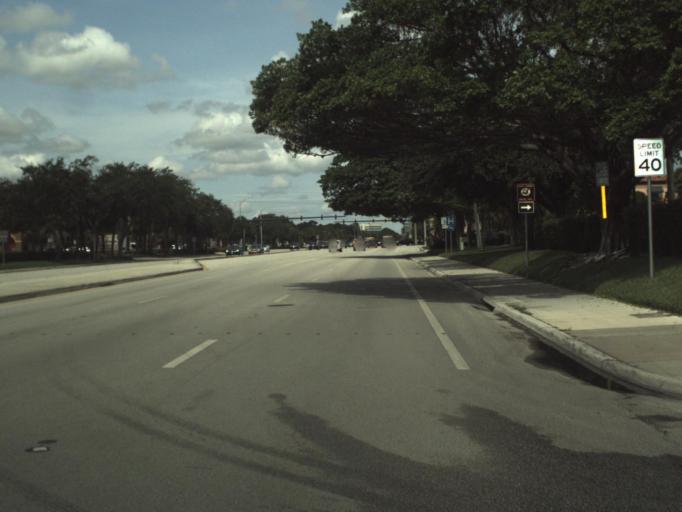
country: US
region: Florida
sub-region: Palm Beach County
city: North Palm Beach
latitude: 26.8447
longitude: -80.0697
